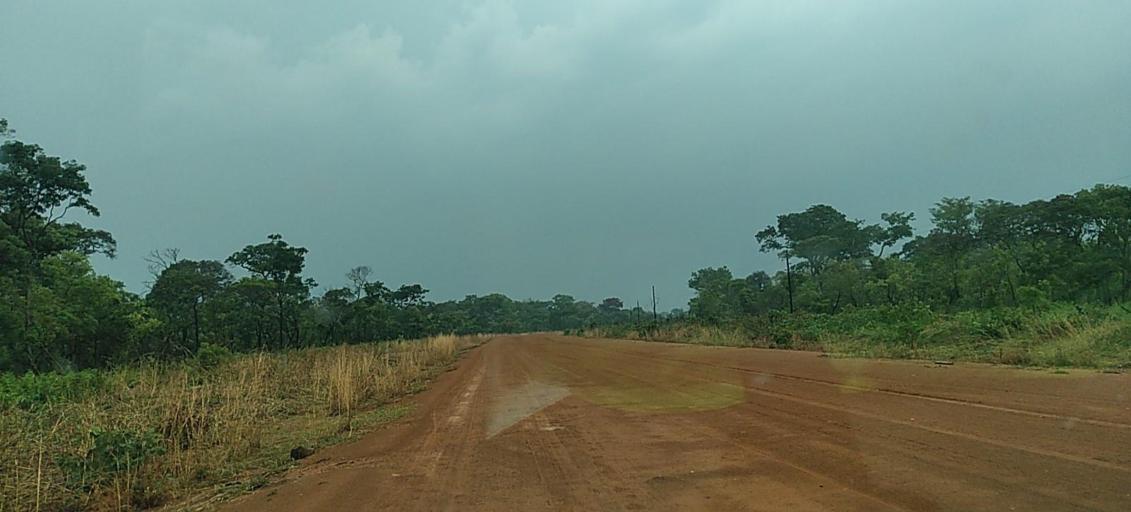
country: ZM
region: North-Western
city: Mwinilunga
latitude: -11.6189
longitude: 24.4020
